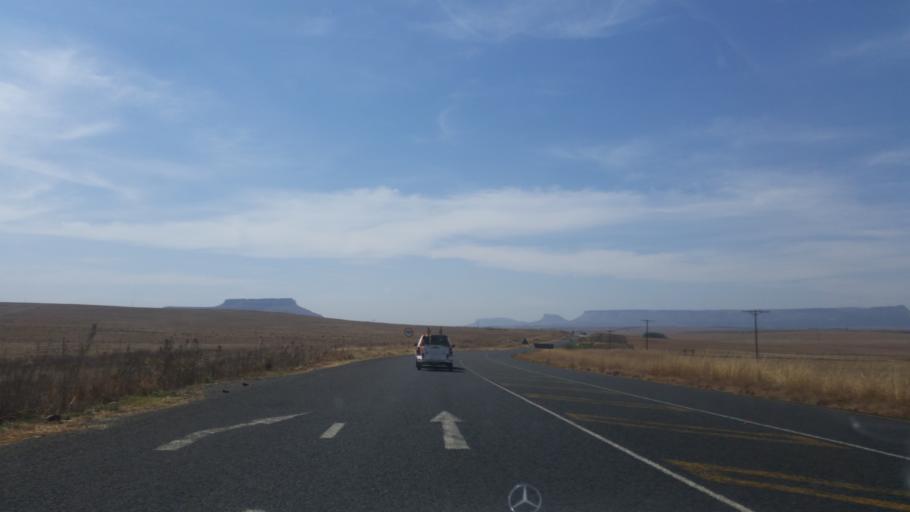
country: ZA
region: Orange Free State
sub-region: Thabo Mofutsanyana District Municipality
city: Harrismith
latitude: -28.4180
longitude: 29.0654
